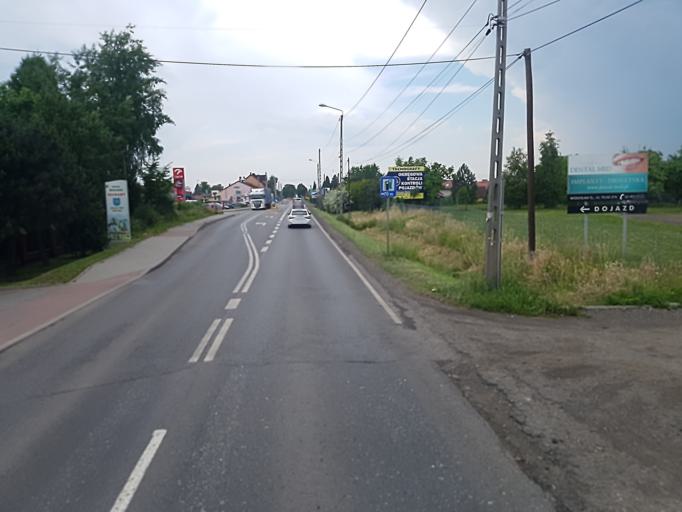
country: PL
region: Silesian Voivodeship
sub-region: Powiat wodzislawski
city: Mszana
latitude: 49.9853
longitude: 18.5071
